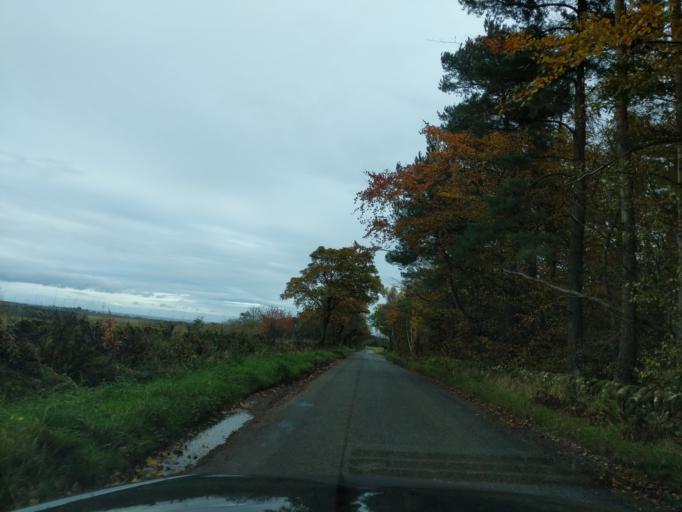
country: GB
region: Scotland
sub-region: Fife
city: Saint Andrews
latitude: 56.2892
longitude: -2.7726
